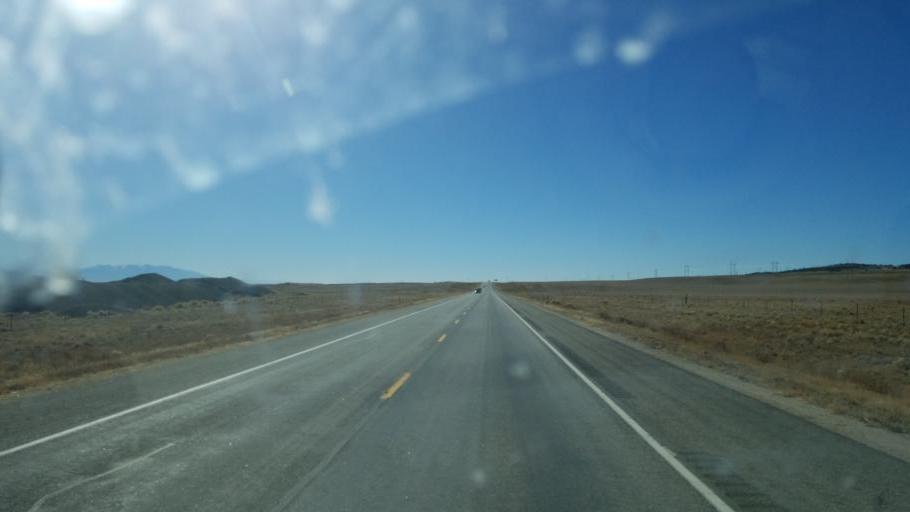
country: US
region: Colorado
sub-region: Saguache County
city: Saguache
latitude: 38.2059
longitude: -105.9424
